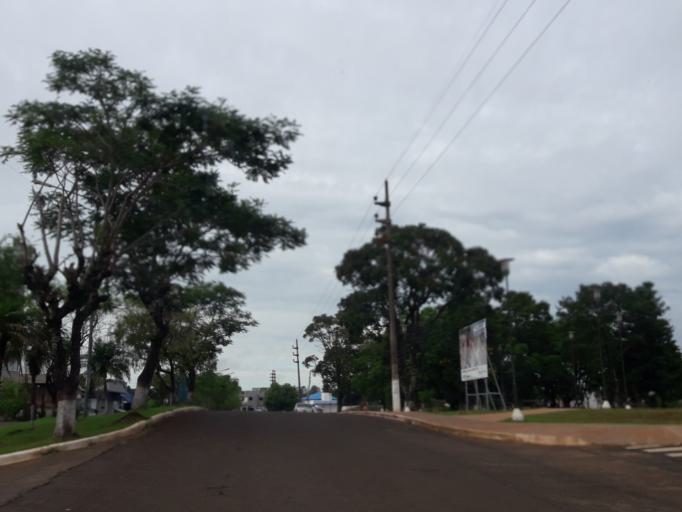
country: AR
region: Misiones
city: Bernardo de Irigoyen
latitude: -26.2553
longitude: -53.6461
